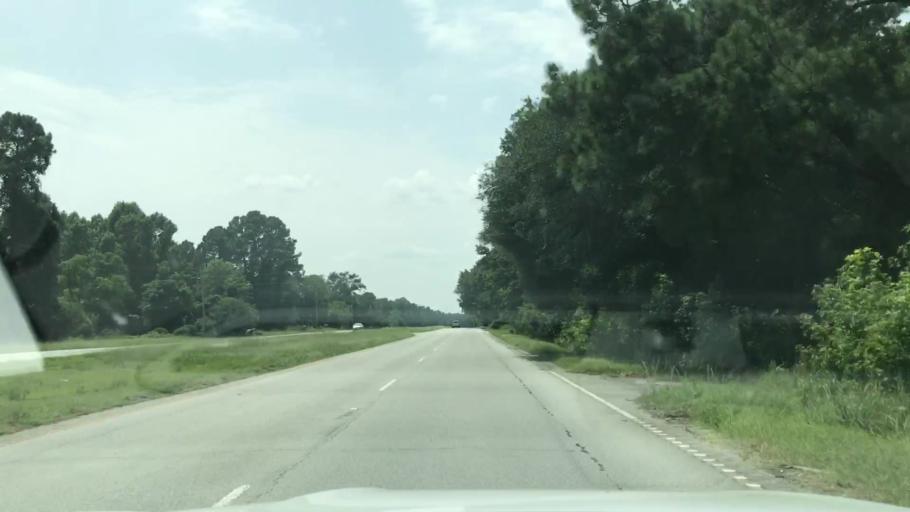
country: US
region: South Carolina
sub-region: Charleston County
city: Awendaw
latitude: 33.0506
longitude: -79.5574
